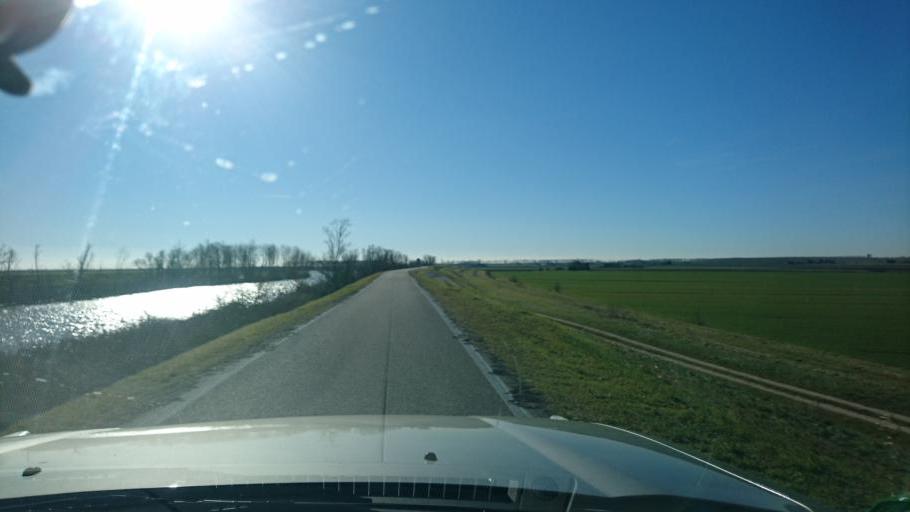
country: IT
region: Veneto
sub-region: Provincia di Rovigo
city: Ariano
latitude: 44.9415
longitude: 12.1655
